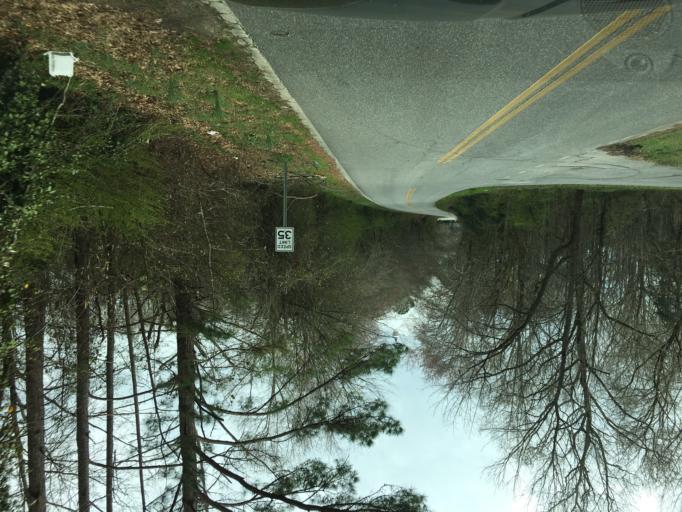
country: US
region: South Carolina
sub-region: Anderson County
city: Pendleton
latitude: 34.6586
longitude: -82.7814
